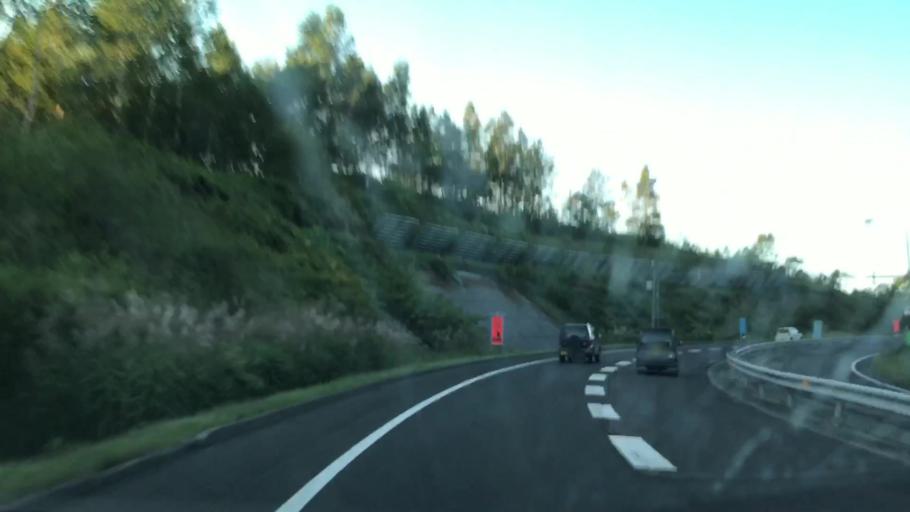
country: JP
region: Hokkaido
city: Otaru
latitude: 42.8481
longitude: 141.0665
